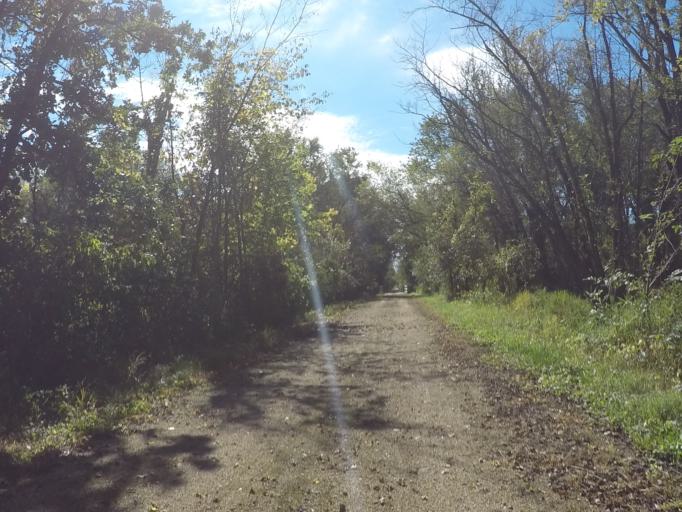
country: US
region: Wisconsin
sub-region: Richland County
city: Richland Center
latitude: 43.2853
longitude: -90.3209
